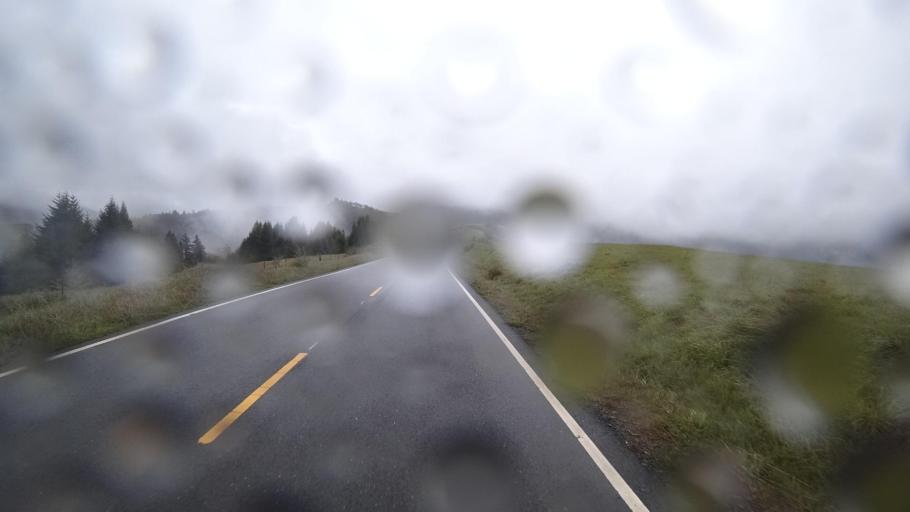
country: US
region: California
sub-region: Humboldt County
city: Westhaven-Moonstone
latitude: 41.1649
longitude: -123.9095
